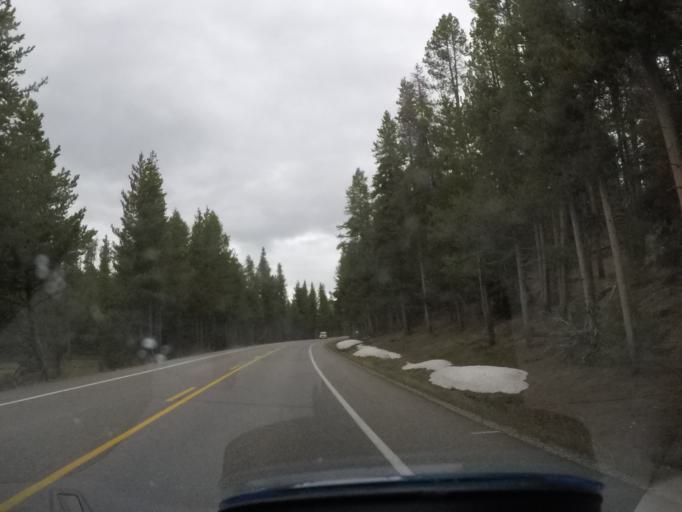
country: US
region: Wyoming
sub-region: Teton County
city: Moose Wilson Road
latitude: 43.9272
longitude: -110.6327
